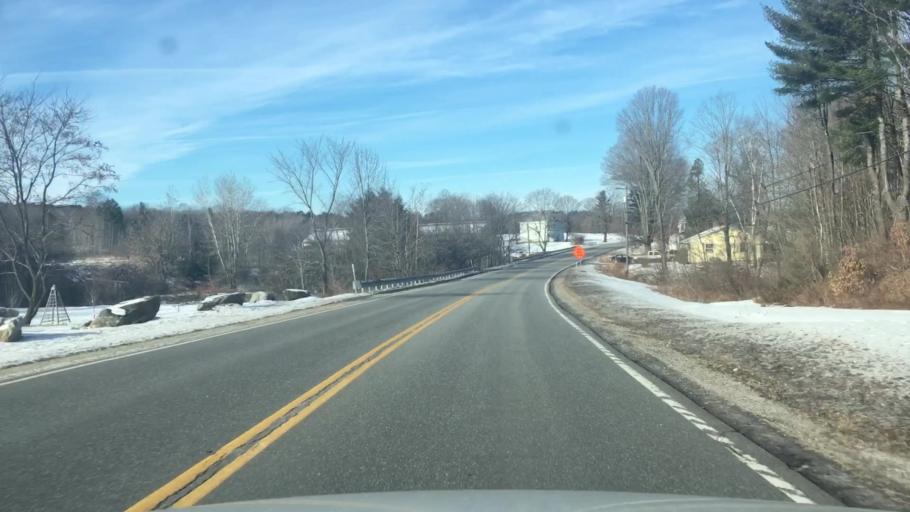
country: US
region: Maine
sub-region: Androscoggin County
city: Lewiston
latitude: 44.0563
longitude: -70.2049
